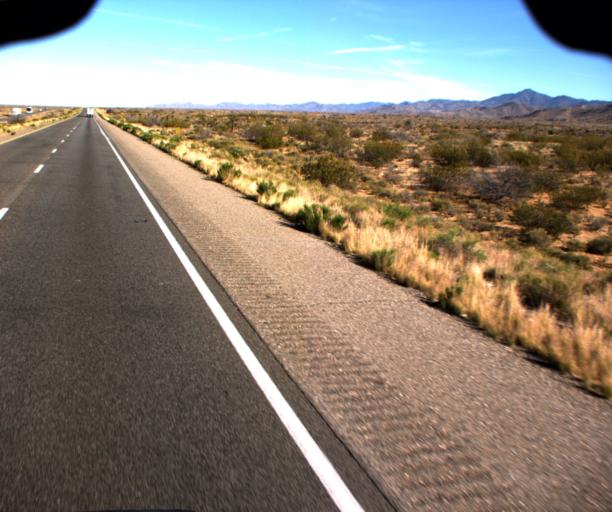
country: US
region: Arizona
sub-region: Mohave County
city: Golden Valley
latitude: 35.2635
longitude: -114.1625
